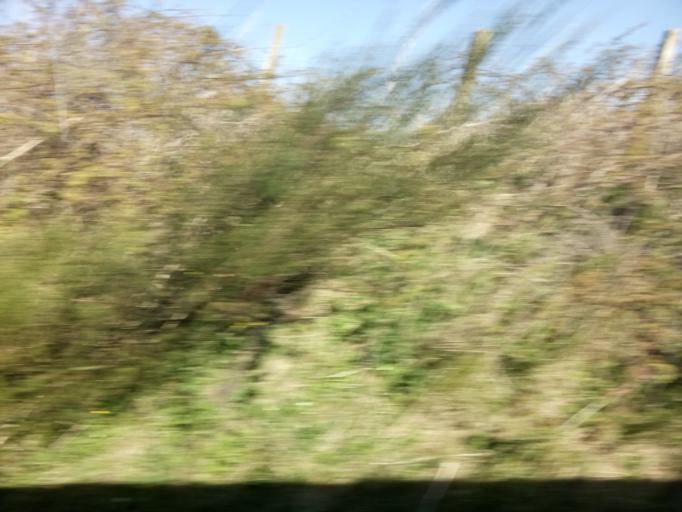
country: GB
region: Scotland
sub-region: Fife
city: Aberdour
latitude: 56.0497
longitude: -3.3324
